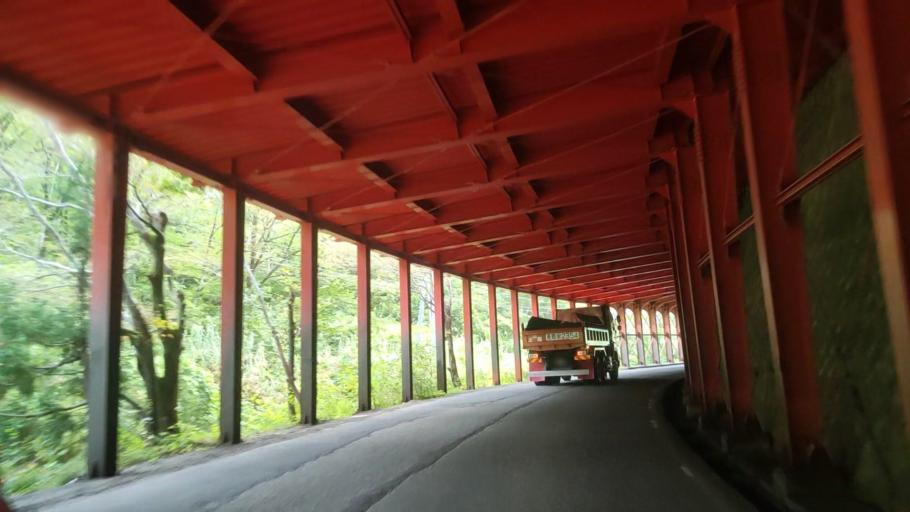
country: JP
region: Nagano
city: Iiyama
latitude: 36.9023
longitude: 138.3173
